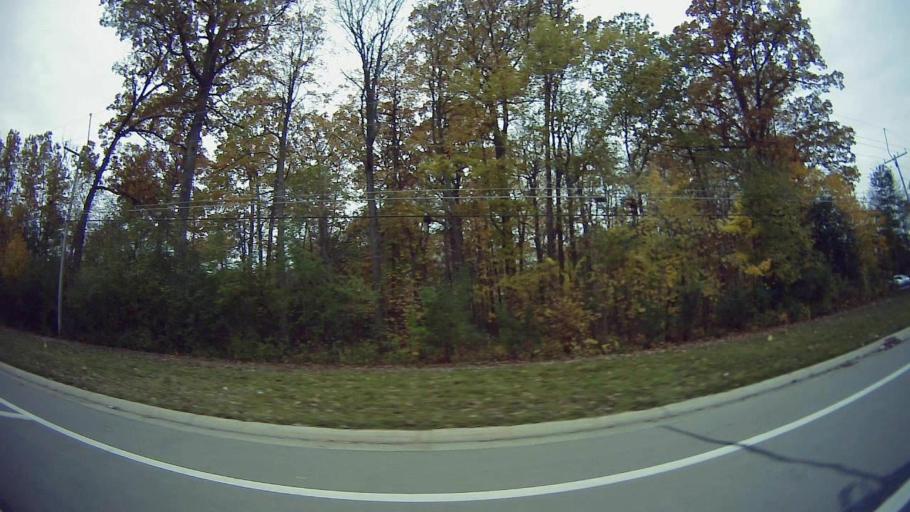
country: US
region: Michigan
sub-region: Oakland County
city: Franklin
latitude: 42.5214
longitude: -83.3444
